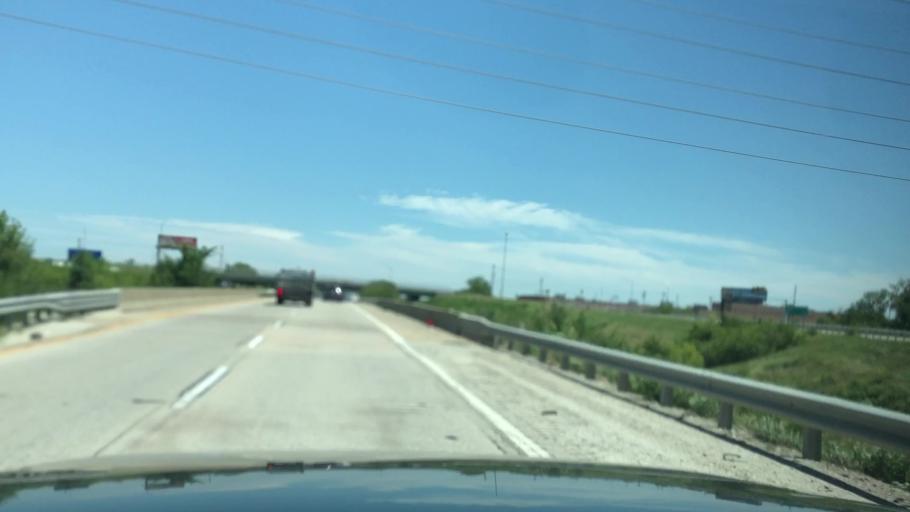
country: US
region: Missouri
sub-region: Saint Louis County
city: Bridgeton
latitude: 38.7707
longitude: -90.4030
